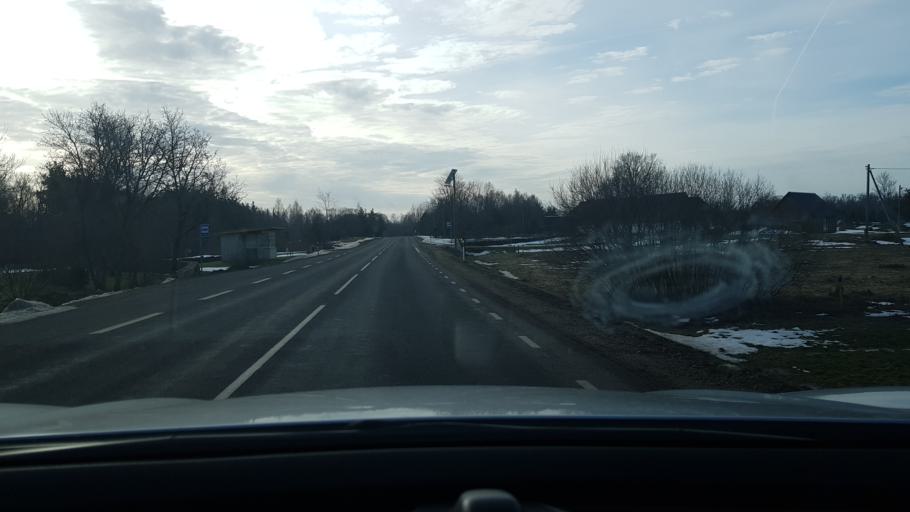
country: EE
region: Saare
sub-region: Kuressaare linn
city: Kuressaare
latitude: 58.3082
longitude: 22.5412
